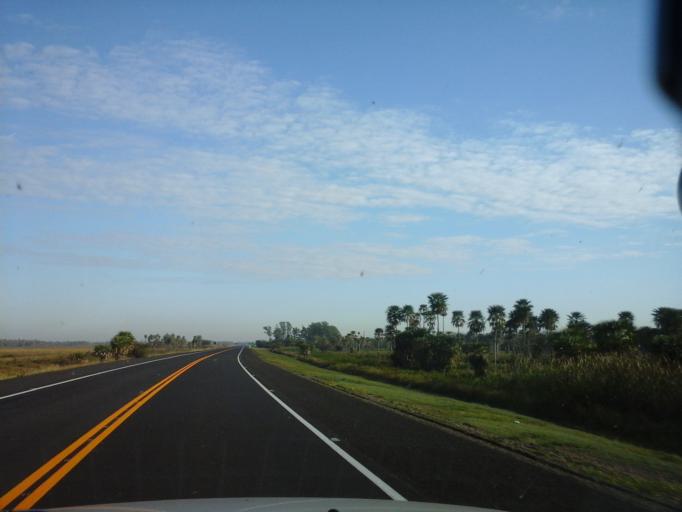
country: PY
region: Neembucu
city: Cerrito
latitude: -26.8833
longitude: -57.7384
